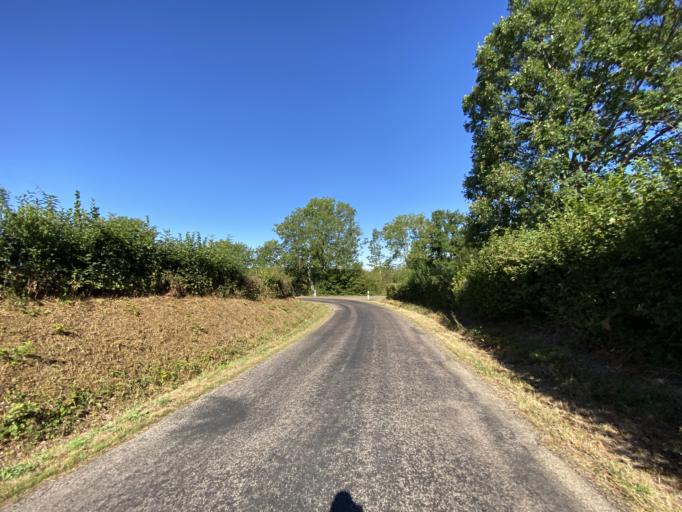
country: FR
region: Bourgogne
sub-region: Departement de la Cote-d'Or
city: Saulieu
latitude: 47.2764
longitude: 4.1849
